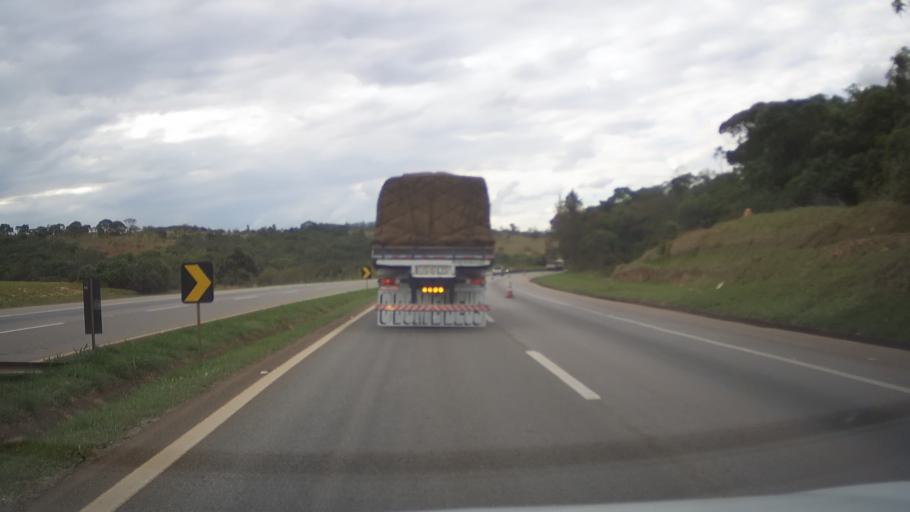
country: BR
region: Minas Gerais
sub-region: Itauna
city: Itauna
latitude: -20.3283
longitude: -44.4550
